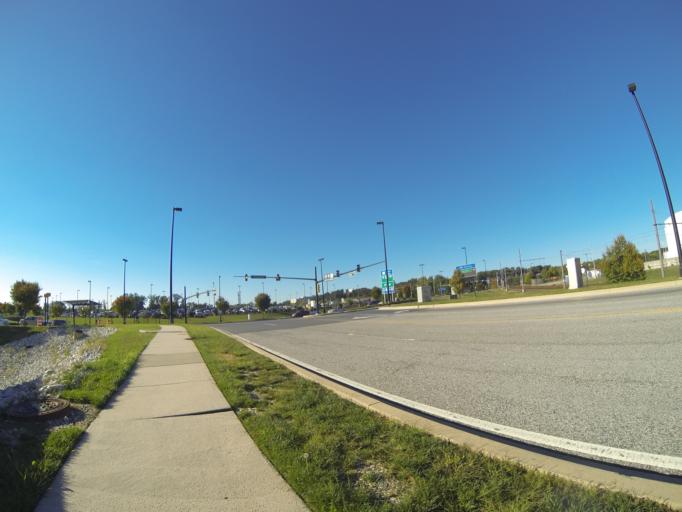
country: US
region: Maryland
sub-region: Anne Arundel County
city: Linthicum
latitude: 39.1887
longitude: -76.6763
